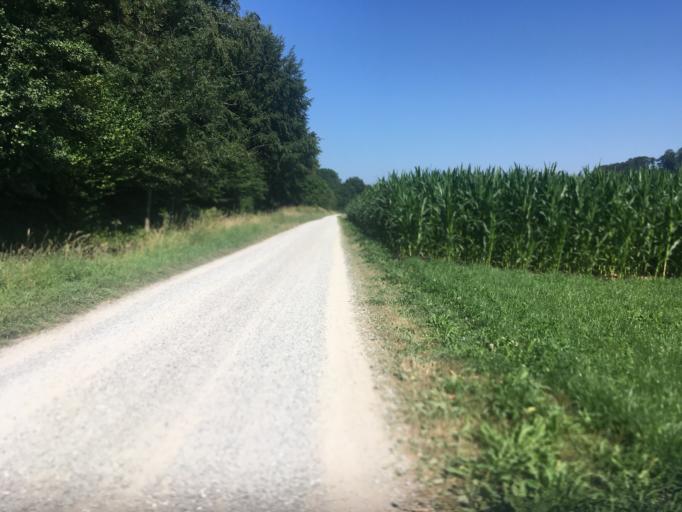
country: CH
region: Bern
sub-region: Emmental District
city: Lyssach
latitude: 47.0728
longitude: 7.5988
